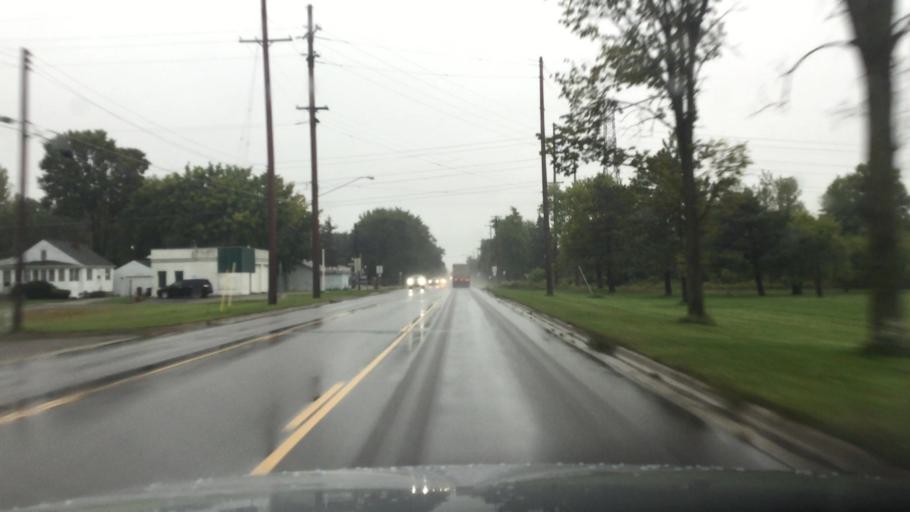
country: US
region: Michigan
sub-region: Saginaw County
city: Saginaw
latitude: 43.3879
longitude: -83.9555
